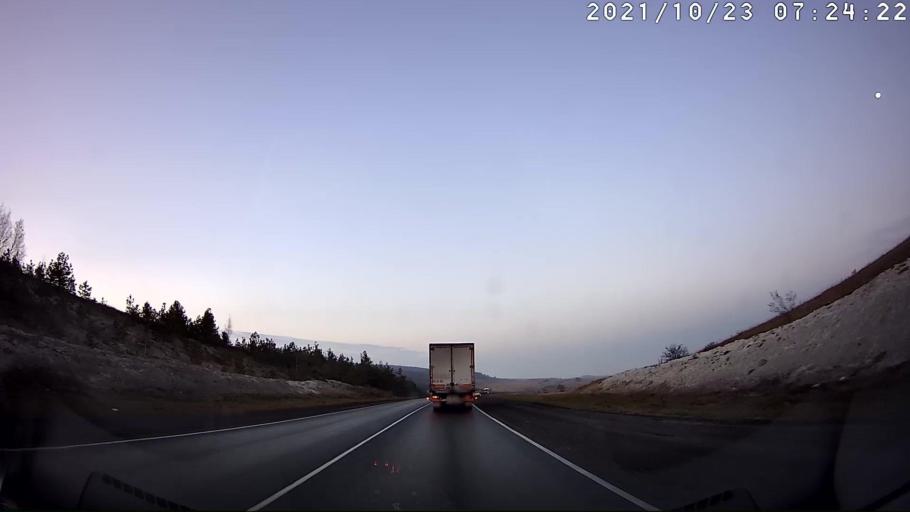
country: RU
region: Saratov
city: Alekseyevka
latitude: 52.3720
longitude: 47.9692
